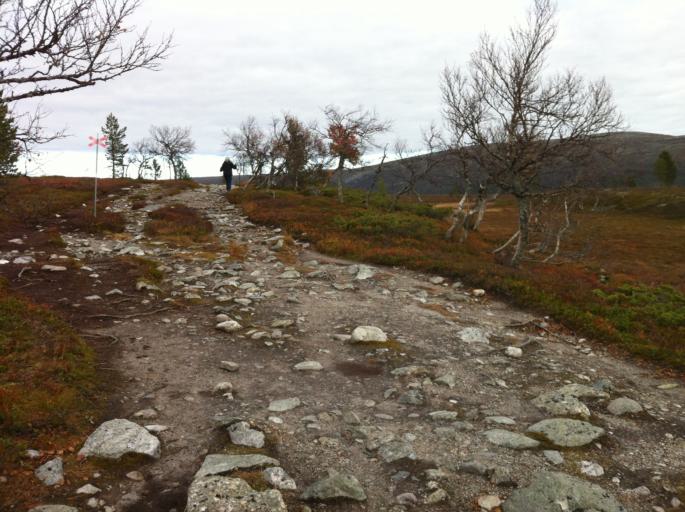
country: NO
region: Hedmark
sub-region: Engerdal
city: Engerdal
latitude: 62.0975
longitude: 12.2659
